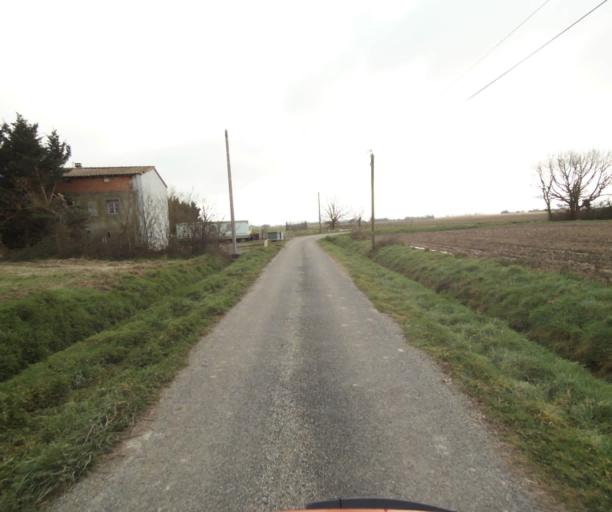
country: FR
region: Midi-Pyrenees
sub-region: Departement de l'Ariege
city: Mazeres
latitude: 43.2011
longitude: 1.6784
